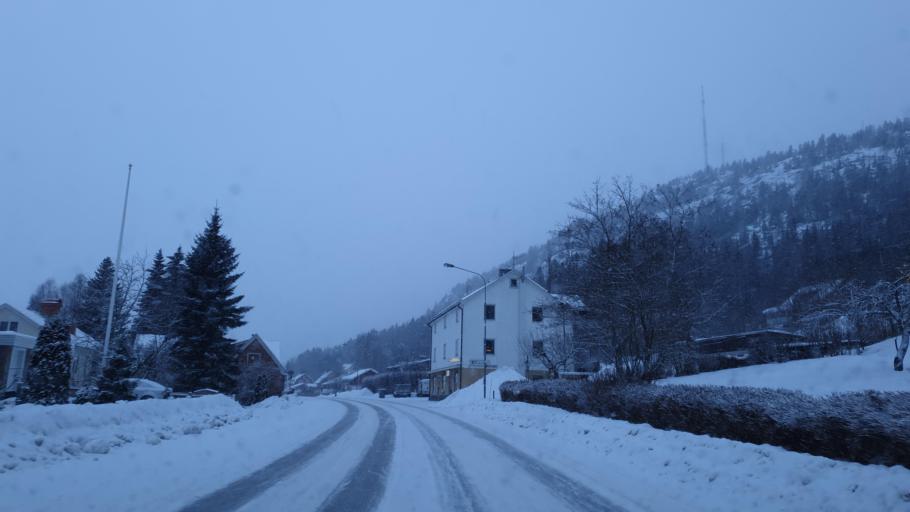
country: SE
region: Vaesternorrland
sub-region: OErnskoeldsviks Kommun
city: Ornskoldsvik
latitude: 63.2980
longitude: 18.6731
